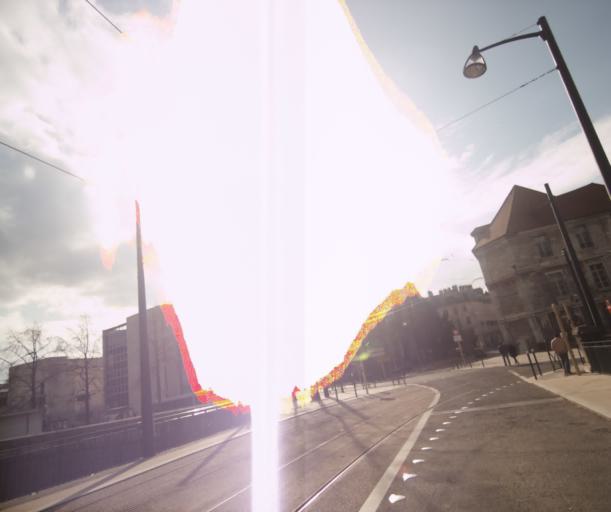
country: FR
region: Franche-Comte
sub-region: Departement du Doubs
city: Besancon
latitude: 47.2410
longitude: 6.0282
